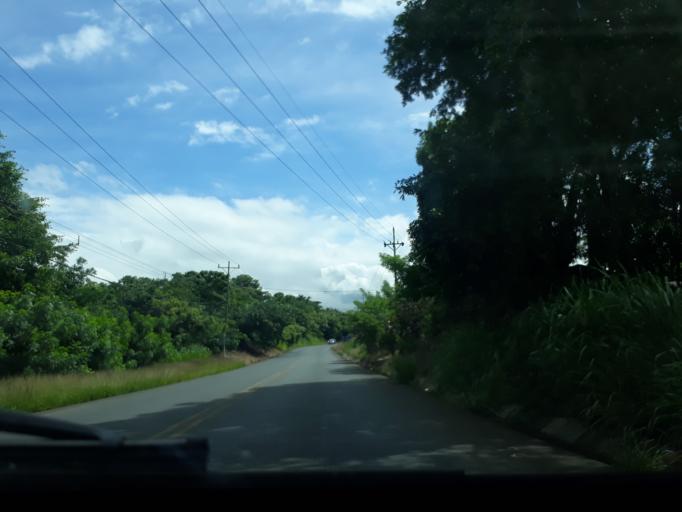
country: CR
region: Alajuela
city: Atenas
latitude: 10.0280
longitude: -84.3564
